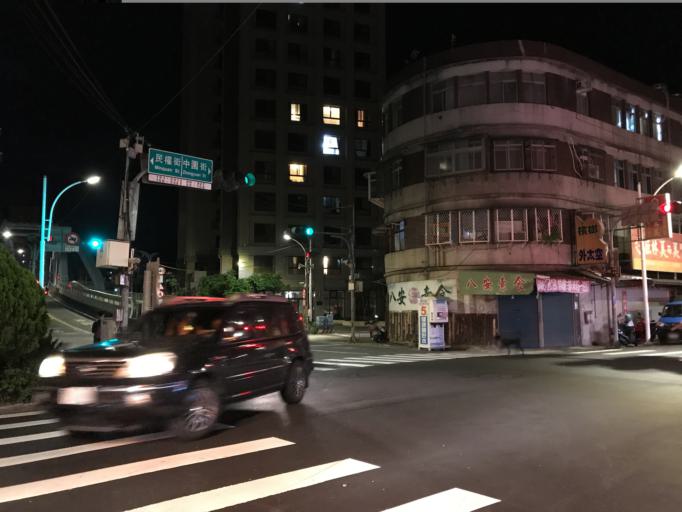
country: TW
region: Taiwan
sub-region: Taoyuan
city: Taoyuan
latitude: 24.9271
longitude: 121.3681
